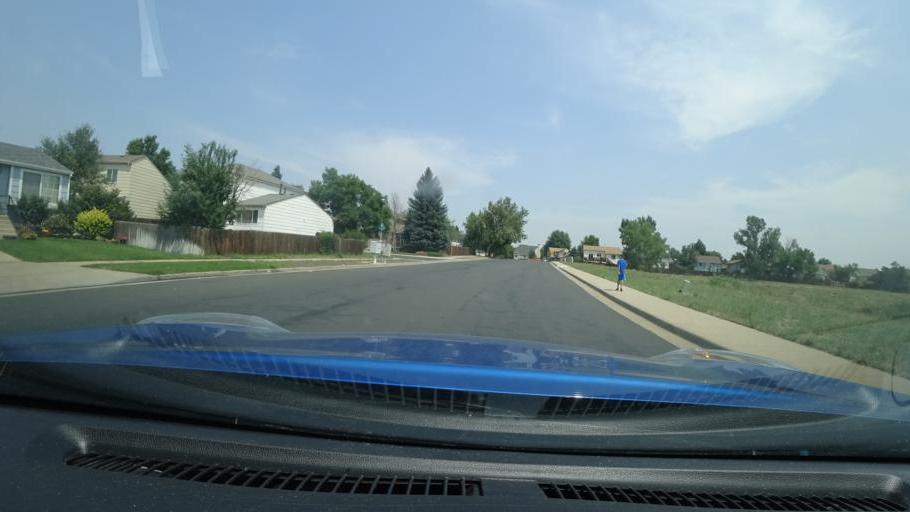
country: US
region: Colorado
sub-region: Adams County
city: Aurora
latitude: 39.7737
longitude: -104.7600
